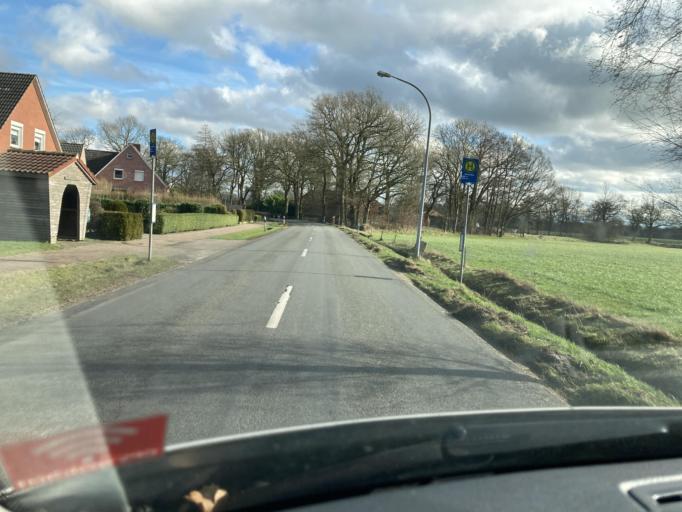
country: DE
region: Lower Saxony
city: Detern
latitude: 53.2501
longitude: 7.6827
